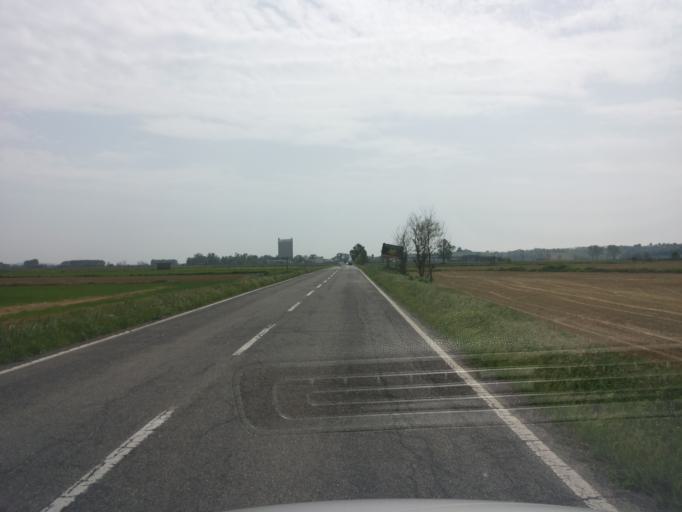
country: IT
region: Piedmont
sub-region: Provincia di Alessandria
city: Terruggia
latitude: 45.0821
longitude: 8.4754
